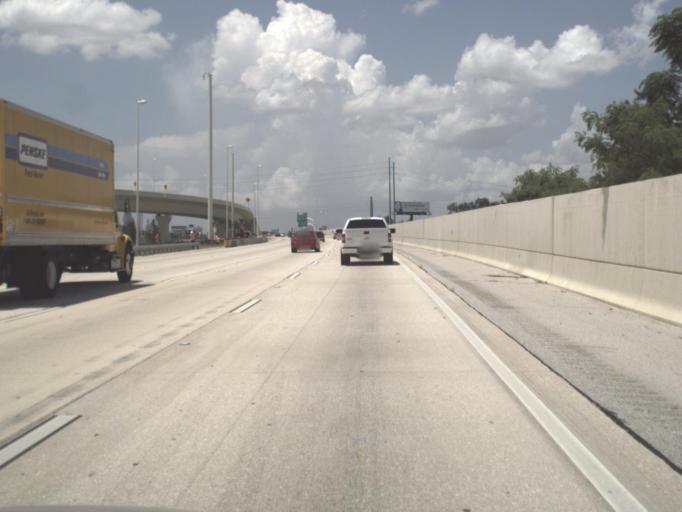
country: US
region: Florida
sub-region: Hillsborough County
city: Tampa
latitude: 27.9656
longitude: -82.4242
